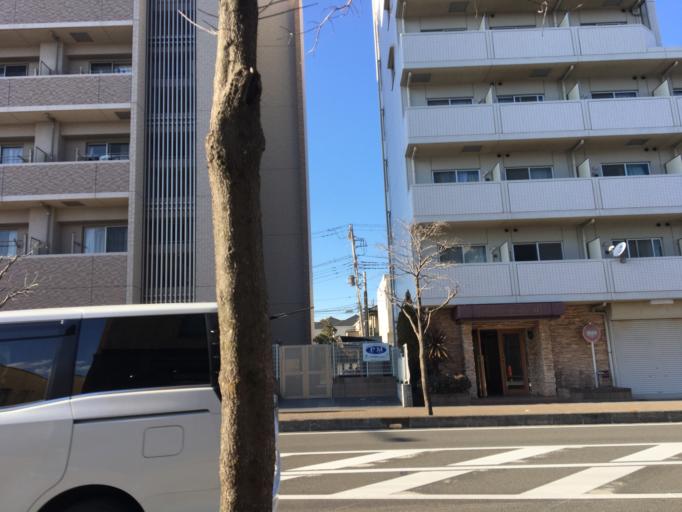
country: JP
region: Saitama
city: Oi
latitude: 35.8443
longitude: 139.5374
